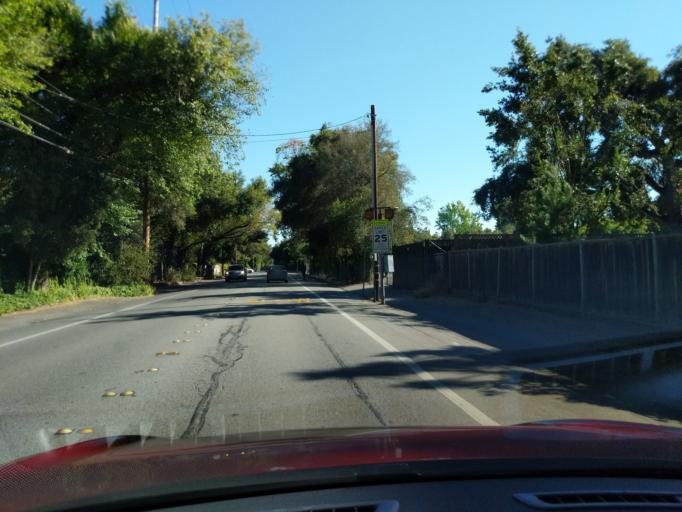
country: US
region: California
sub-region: San Mateo County
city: Menlo Park
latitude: 37.4672
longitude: -122.1701
